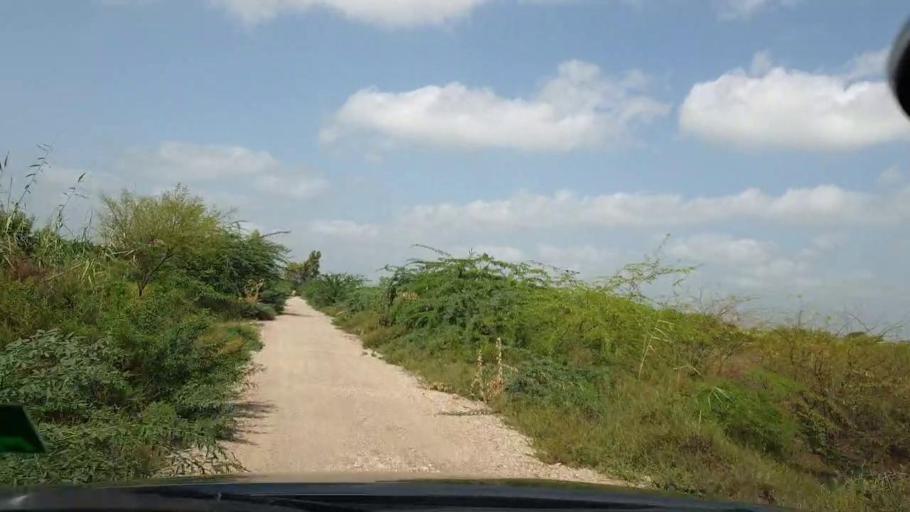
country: PK
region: Sindh
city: Kadhan
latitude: 24.5918
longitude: 69.1130
